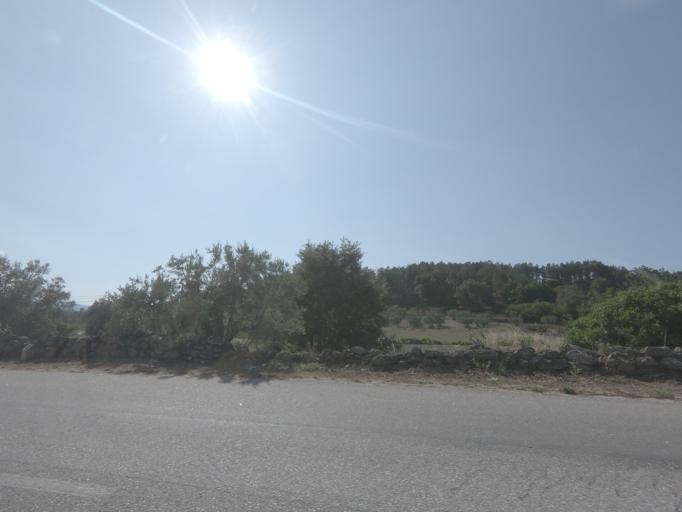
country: PT
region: Viseu
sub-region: Moimenta da Beira
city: Moimenta da Beira
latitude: 40.9936
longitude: -7.5609
